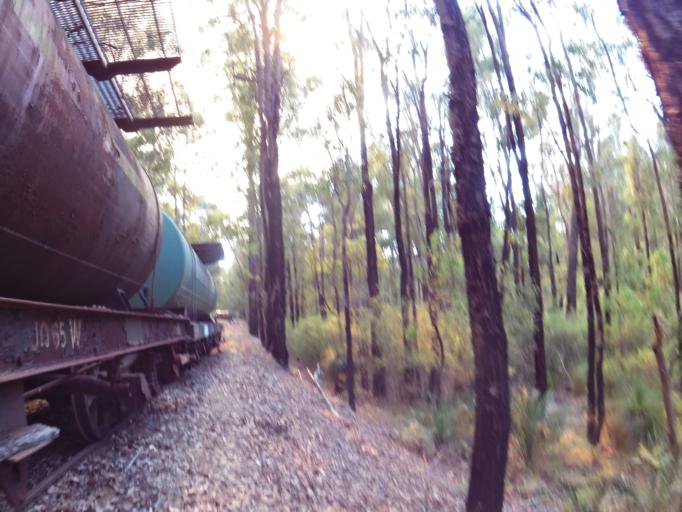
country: AU
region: Western Australia
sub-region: Waroona
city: Waroona
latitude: -32.7393
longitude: 116.1410
